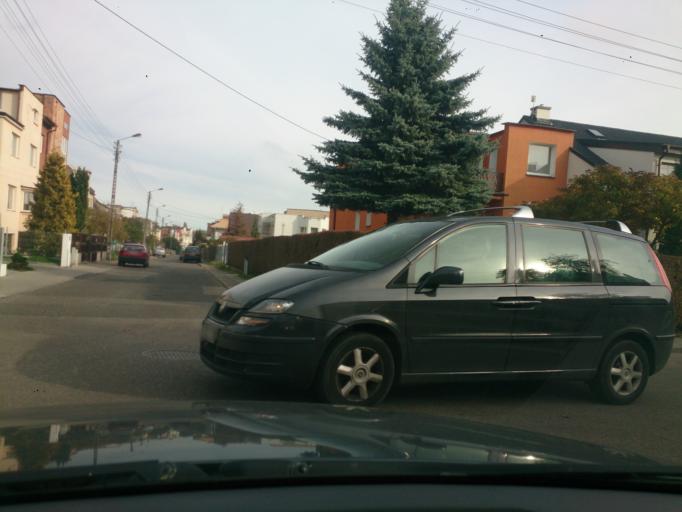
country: PL
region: Pomeranian Voivodeship
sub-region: Gdynia
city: Wielki Kack
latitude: 54.4857
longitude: 18.5172
